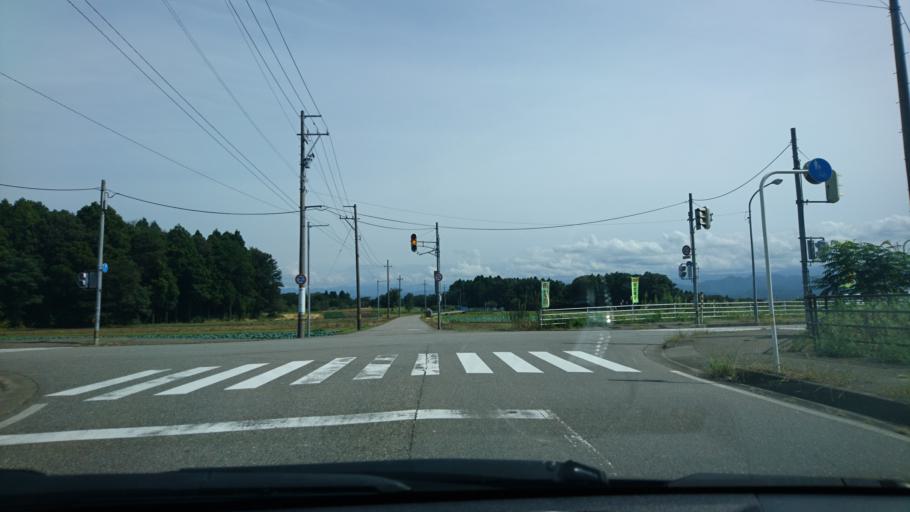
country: JP
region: Ishikawa
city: Komatsu
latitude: 36.3305
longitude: 136.3538
